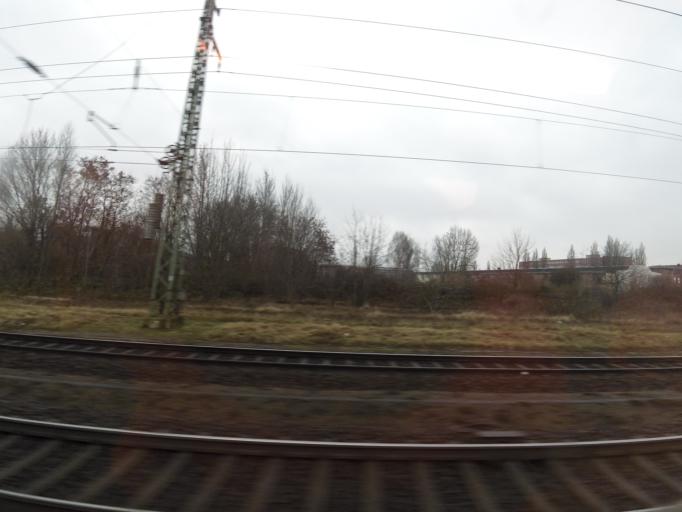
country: DE
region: Saxony-Anhalt
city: Magdeburg
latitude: 52.1197
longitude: 11.6035
